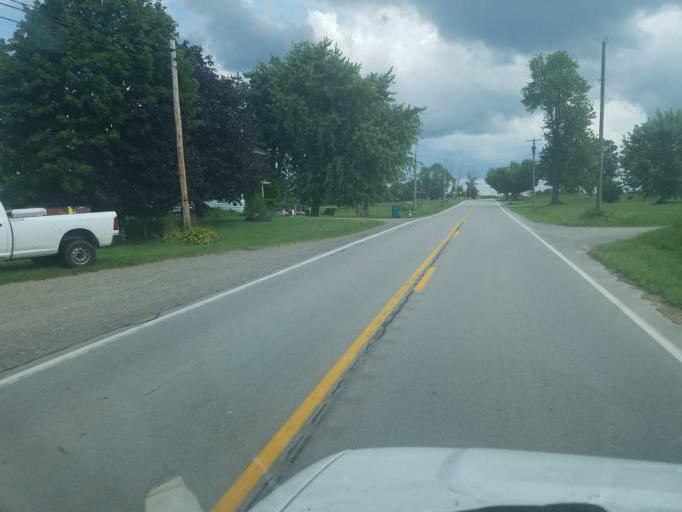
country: US
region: Pennsylvania
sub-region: Crawford County
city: Conneaut Lakeshore
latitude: 41.5844
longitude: -80.3005
